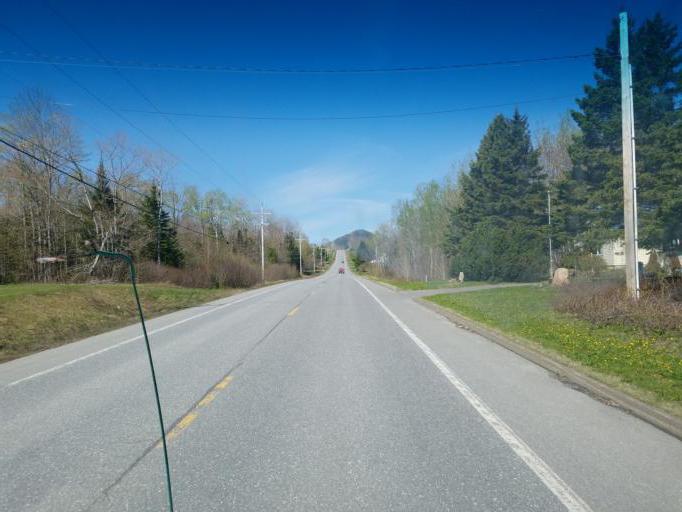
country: US
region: Maine
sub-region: Aroostook County
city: Presque Isle
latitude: 46.6669
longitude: -68.2023
